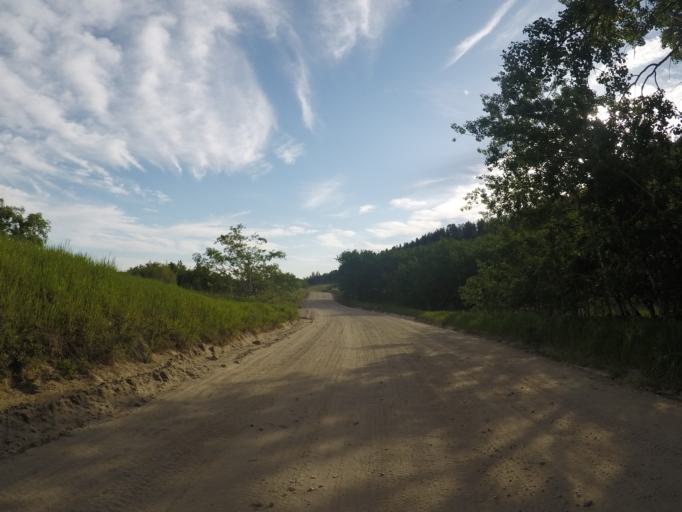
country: US
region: Montana
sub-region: Stillwater County
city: Absarokee
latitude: 45.2991
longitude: -109.5304
